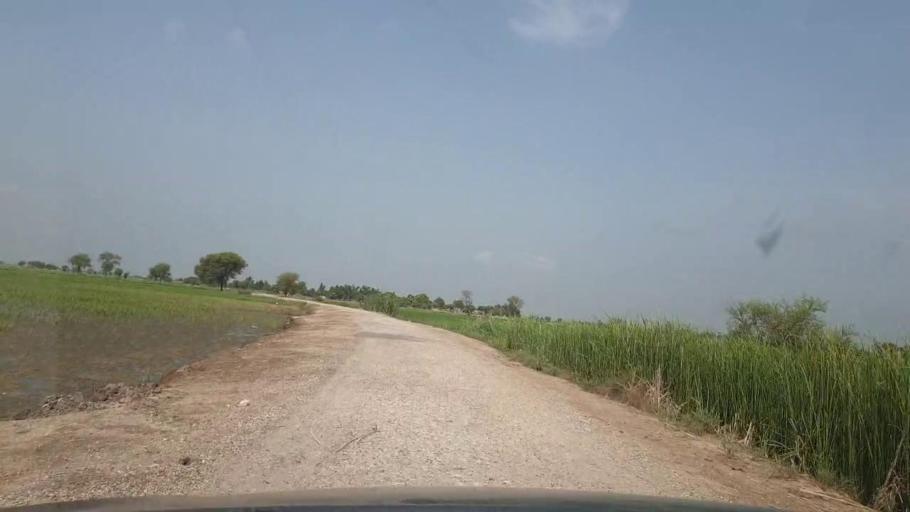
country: PK
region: Sindh
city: Ratodero
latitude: 27.8736
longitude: 68.3189
